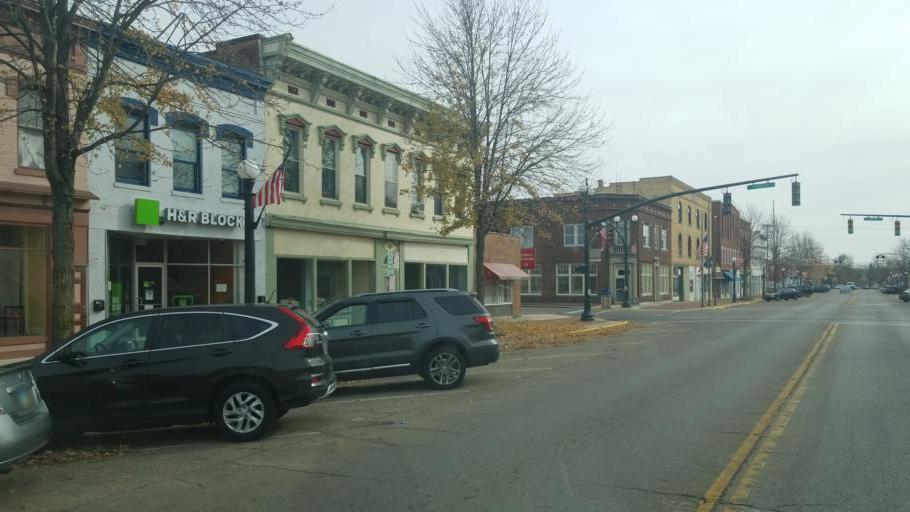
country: US
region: Ohio
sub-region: Madison County
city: London
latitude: 39.8852
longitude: -83.4473
